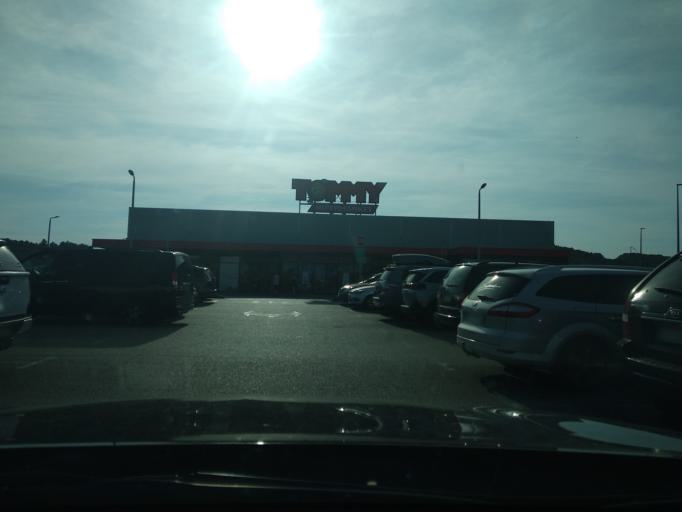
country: HR
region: Sibensko-Kniniska
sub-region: Grad Sibenik
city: Tisno
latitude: 43.7894
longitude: 15.6312
